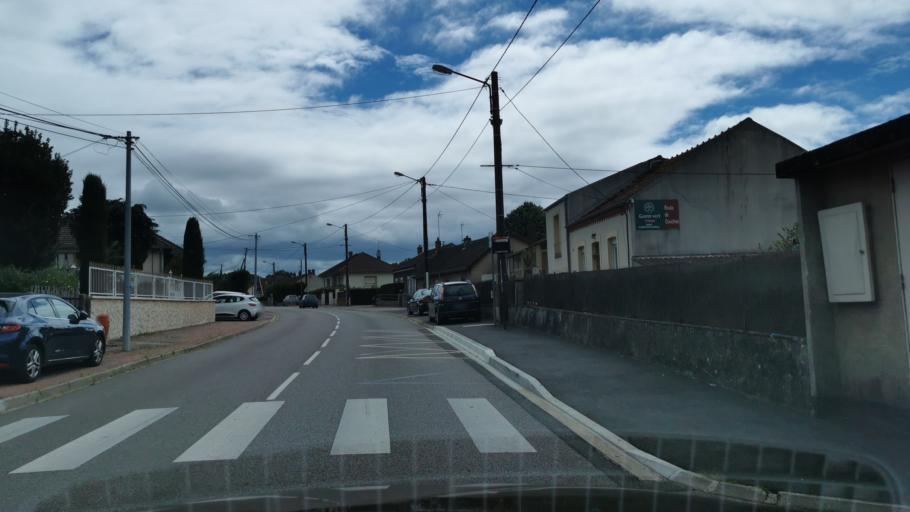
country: FR
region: Bourgogne
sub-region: Departement de Saone-et-Loire
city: Le Breuil
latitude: 46.8101
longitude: 4.4775
